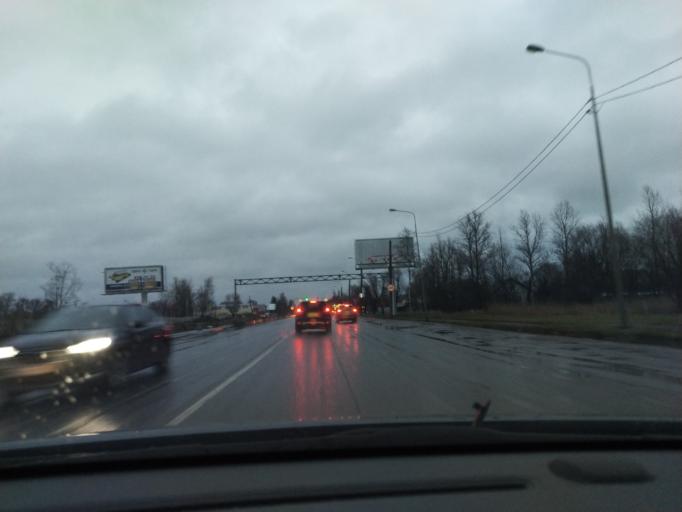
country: RU
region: St.-Petersburg
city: Uritsk
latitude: 59.8115
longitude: 30.1705
